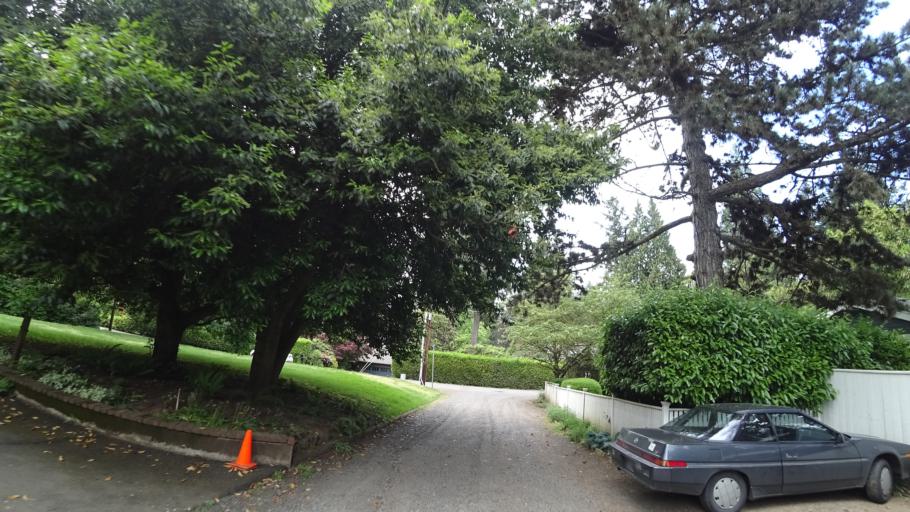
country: US
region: Oregon
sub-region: Clackamas County
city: Milwaukie
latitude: 45.4502
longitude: -122.6609
